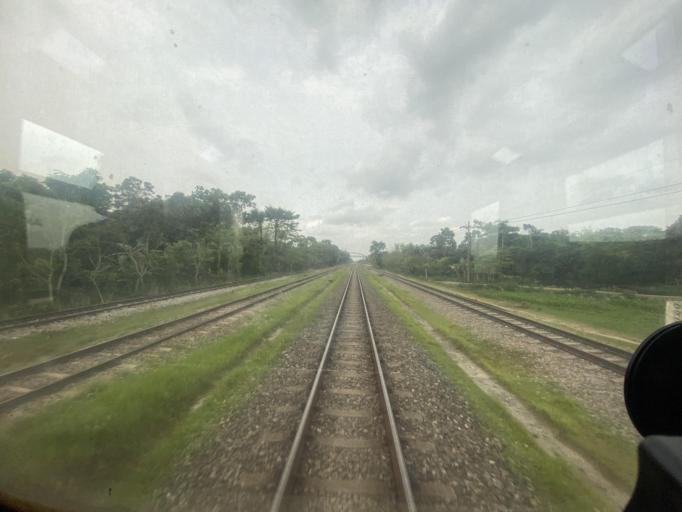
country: BD
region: Chittagong
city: Laksham
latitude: 23.1992
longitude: 91.1612
